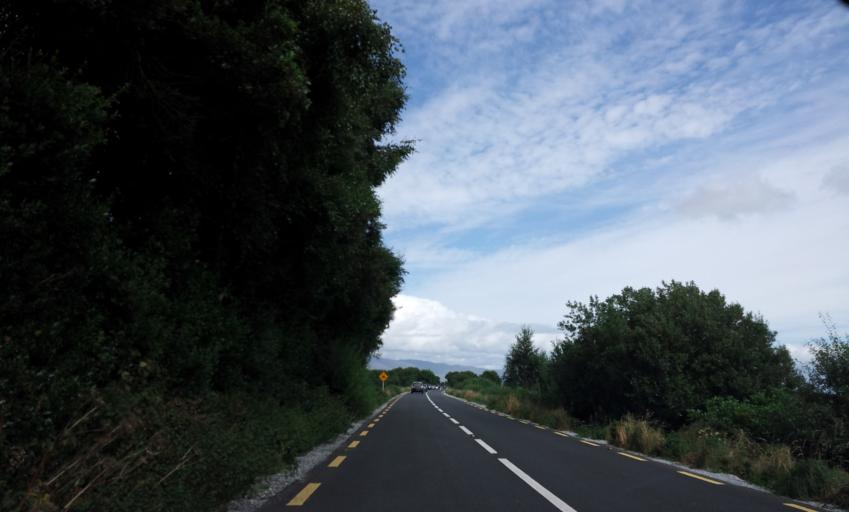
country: IE
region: Munster
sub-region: Ciarrai
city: Killorglin
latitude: 52.0735
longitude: -9.8816
